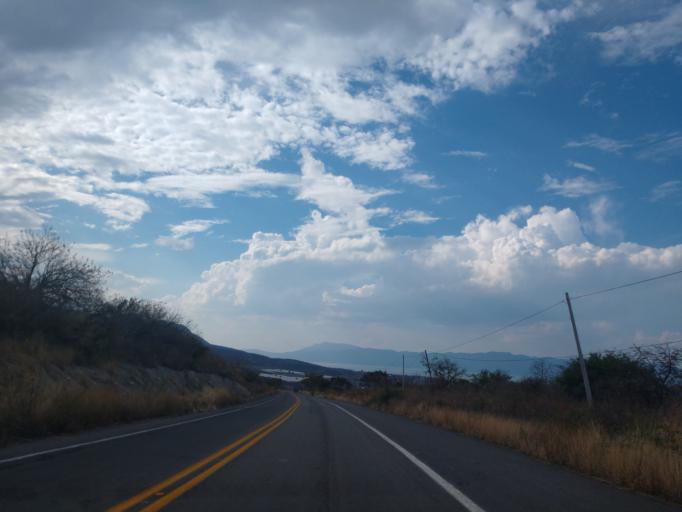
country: MX
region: Jalisco
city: Tizapan el Alto
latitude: 20.1323
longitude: -103.1680
